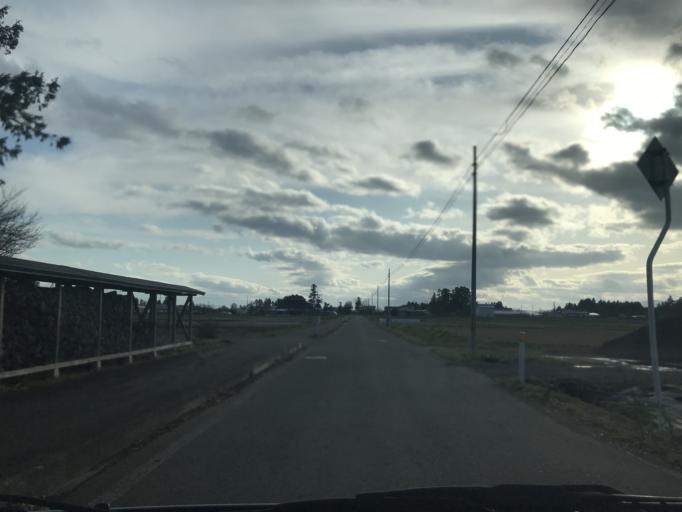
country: JP
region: Iwate
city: Mizusawa
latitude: 39.1905
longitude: 141.1038
